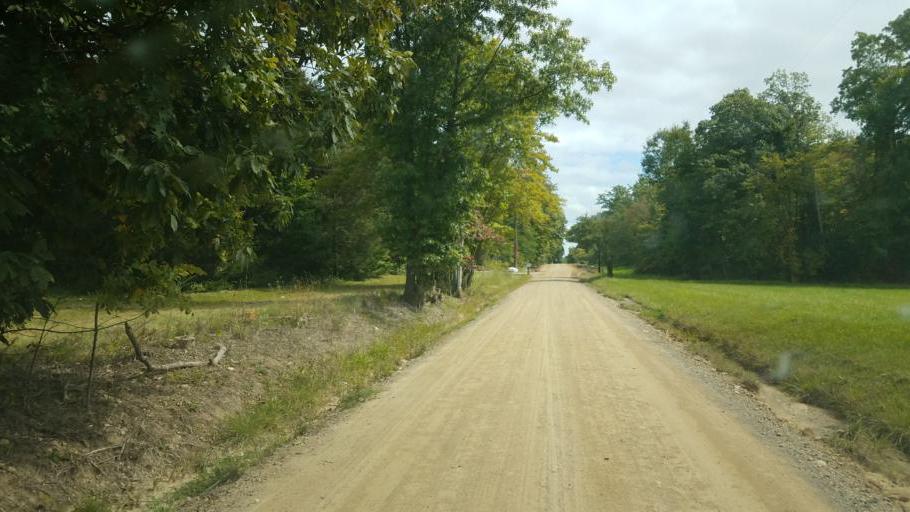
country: US
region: Pennsylvania
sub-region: Mercer County
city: Greenville
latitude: 41.4842
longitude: -80.3235
